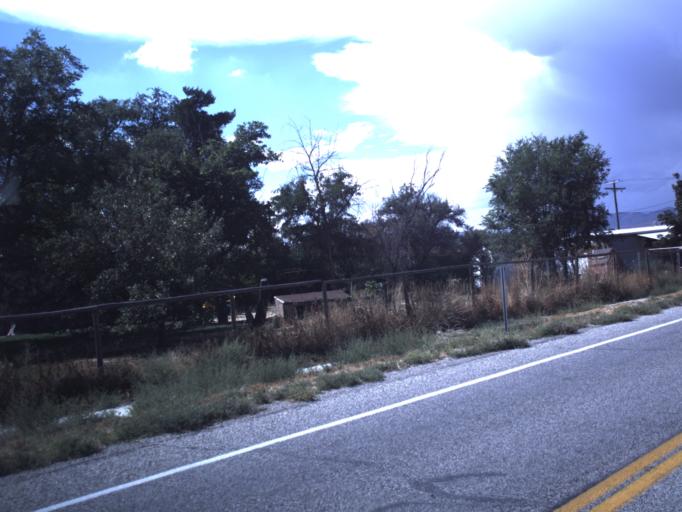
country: US
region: Utah
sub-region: Box Elder County
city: Honeyville
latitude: 41.6450
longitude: -112.0839
